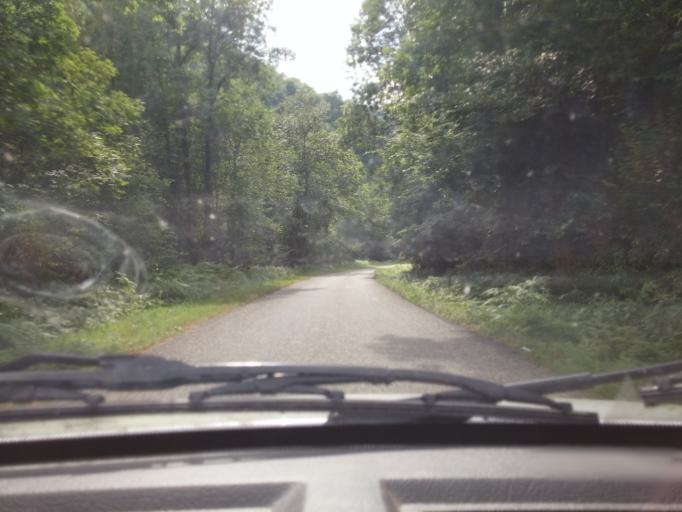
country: FR
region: Midi-Pyrenees
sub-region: Departement de l'Ariege
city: Saint-Girons
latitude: 42.9139
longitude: 1.1959
